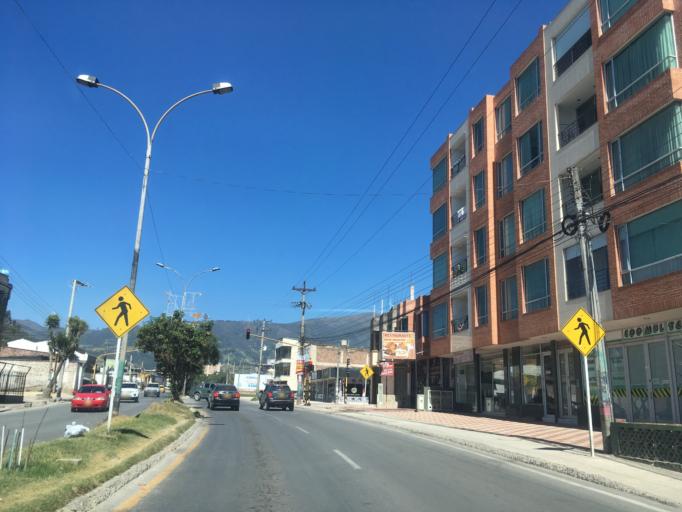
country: CO
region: Boyaca
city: Duitama
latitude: 5.8201
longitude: -73.0242
